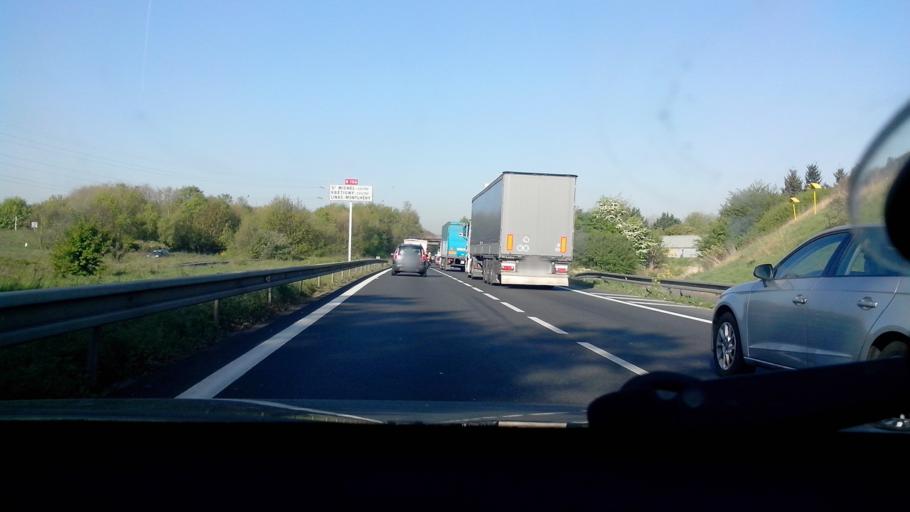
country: FR
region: Ile-de-France
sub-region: Departement de l'Essonne
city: Saint-Michel-sur-Orge
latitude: 48.6255
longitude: 2.3176
